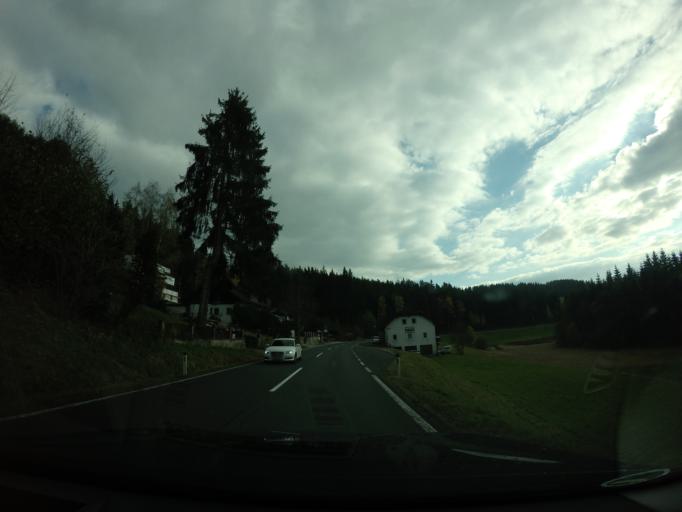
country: AT
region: Upper Austria
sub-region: Politischer Bezirk Urfahr-Umgebung
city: Sonnberg im Muehlkreis
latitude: 48.4827
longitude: 14.2977
